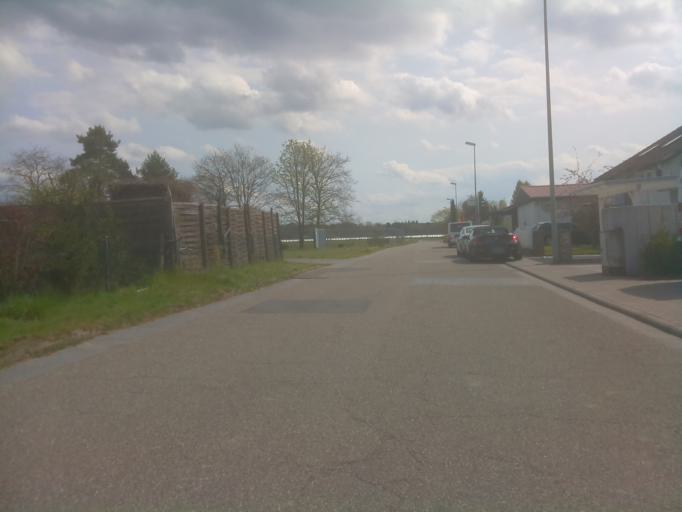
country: DE
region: Hesse
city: Lampertheim
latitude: 49.5811
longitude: 8.4907
